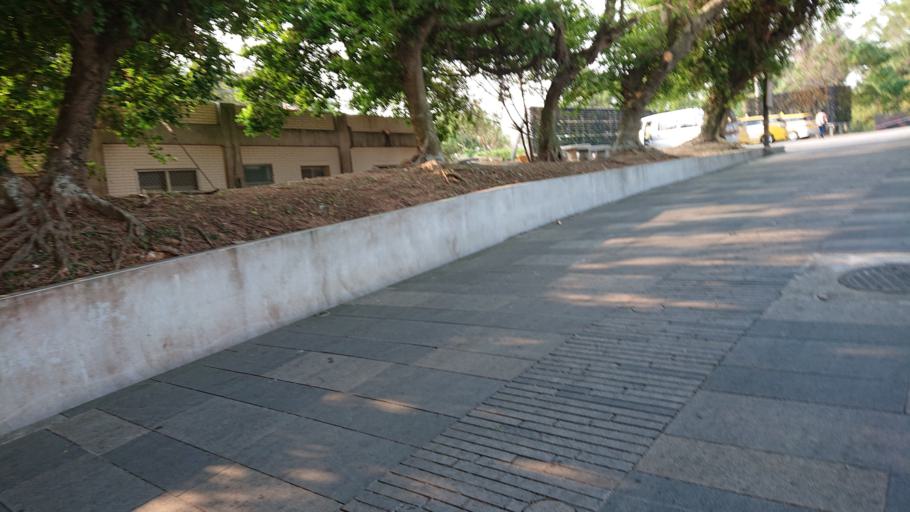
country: TW
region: Fukien
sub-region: Kinmen
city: Jincheng
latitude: 24.4468
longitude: 118.2521
